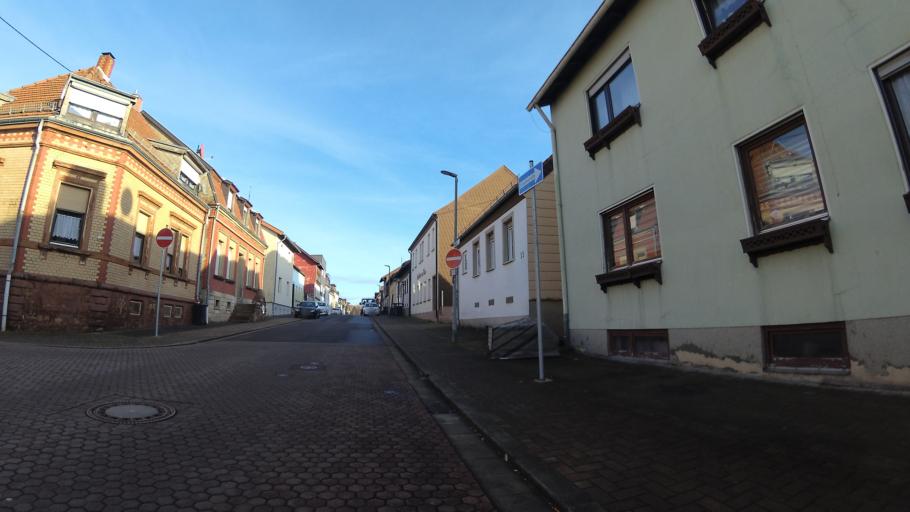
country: DE
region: Saarland
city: Spiesen-Elversberg
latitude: 49.3154
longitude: 7.1334
